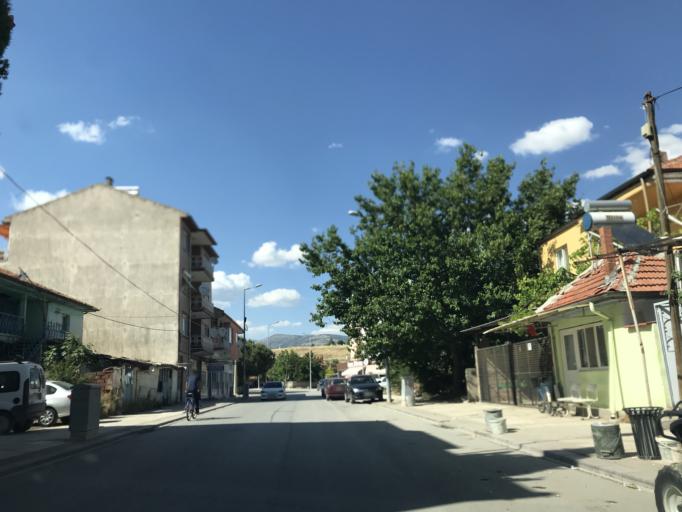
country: TR
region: Denizli
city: Civril
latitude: 38.3035
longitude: 29.7408
